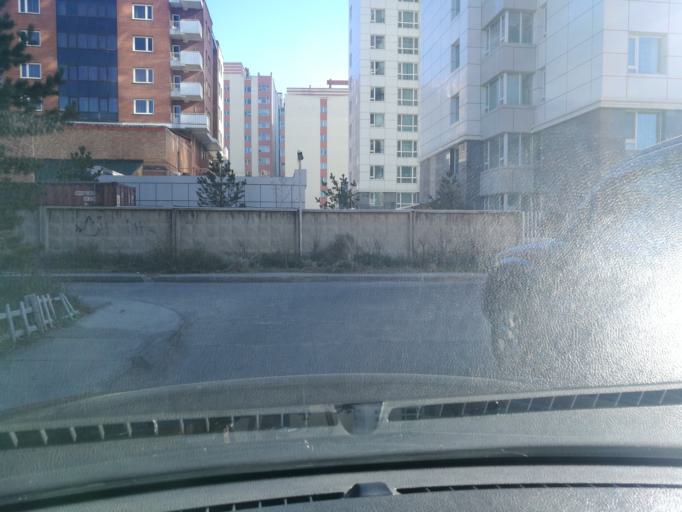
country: MN
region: Ulaanbaatar
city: Ulaanbaatar
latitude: 47.9051
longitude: 106.9094
